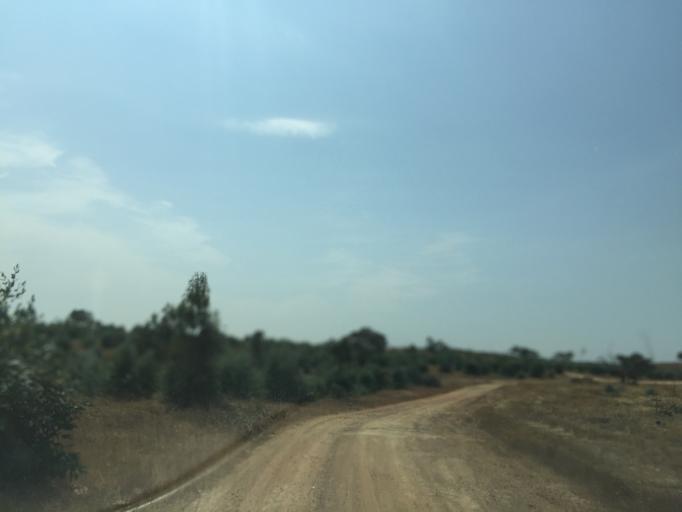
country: PT
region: Setubal
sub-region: Grandola
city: Grandola
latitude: 38.0478
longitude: -8.4654
